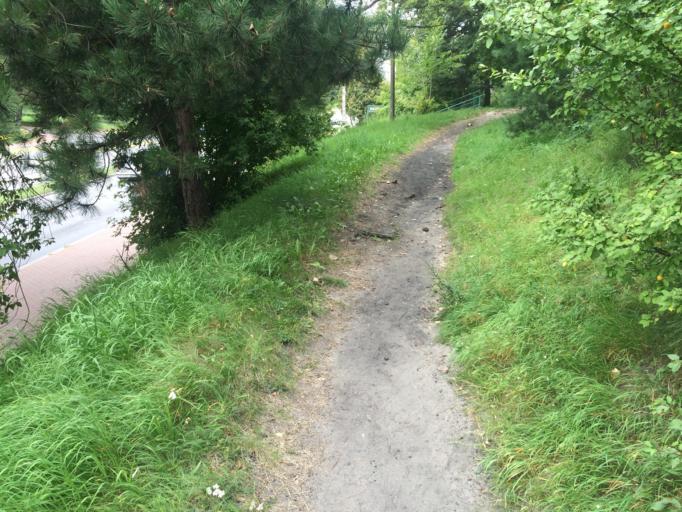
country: PL
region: Swietokrzyskie
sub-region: Powiat starachowicki
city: Starachowice
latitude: 51.0512
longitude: 21.0639
